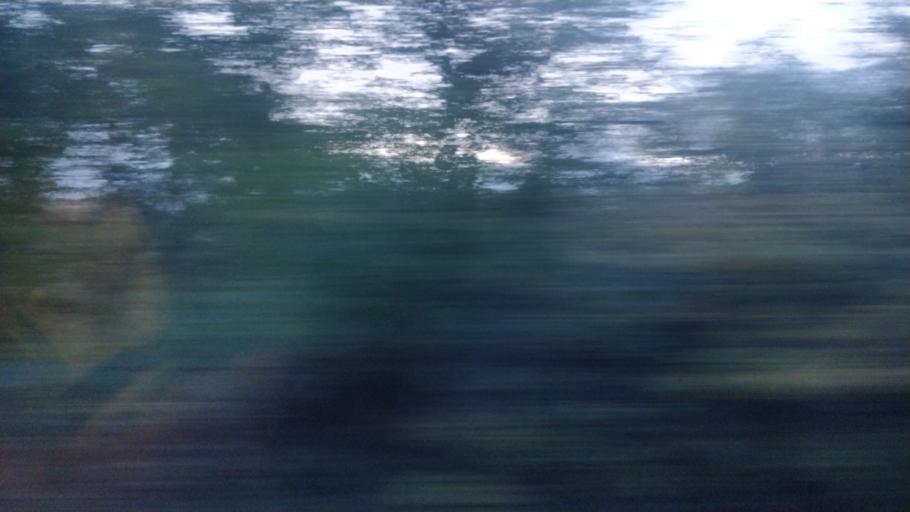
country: GB
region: England
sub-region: Lancashire
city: Appley Bridge
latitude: 53.5688
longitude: -2.7115
